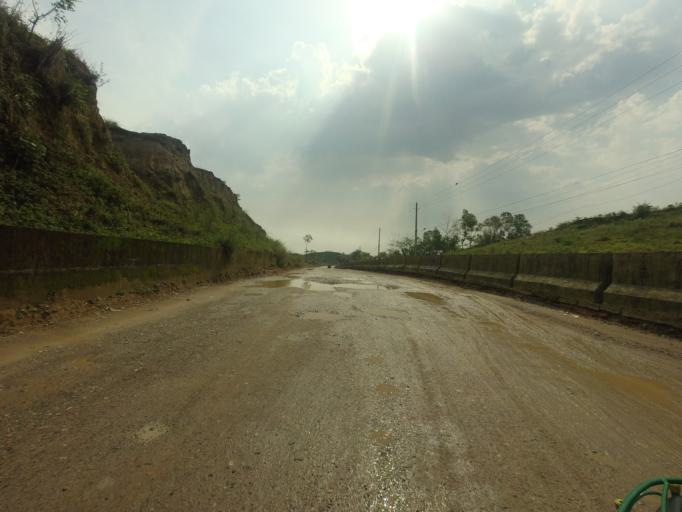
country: BD
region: Sylhet
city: Sylhet
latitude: 24.9521
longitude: 91.8703
